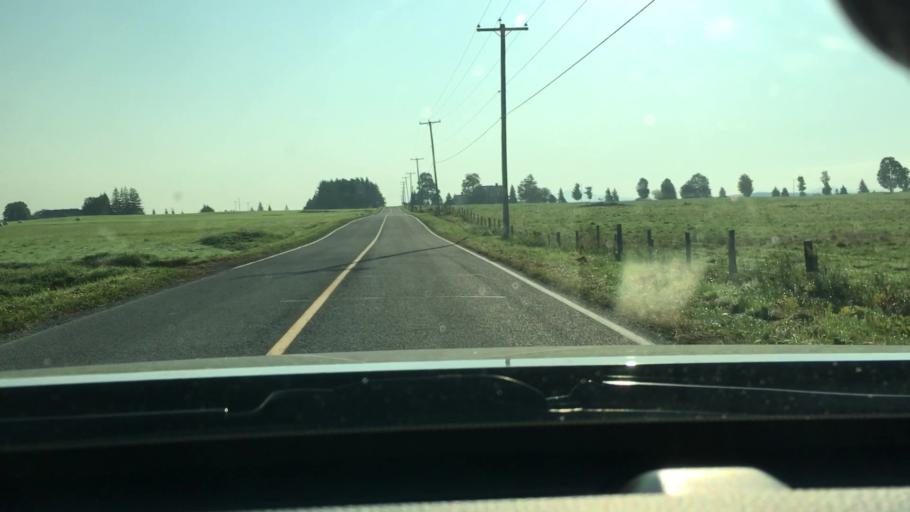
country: CA
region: Quebec
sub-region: Monteregie
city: Waterloo
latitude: 45.3558
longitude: -72.4964
